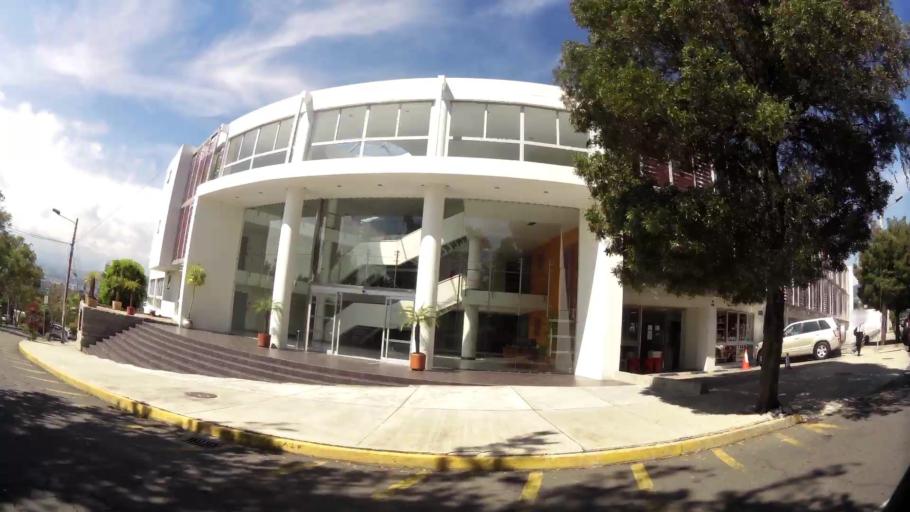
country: EC
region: Pichincha
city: Quito
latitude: -0.1954
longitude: -78.4333
